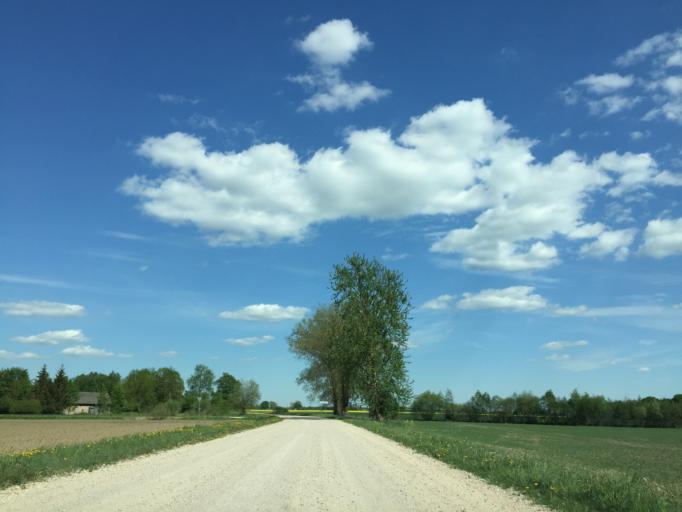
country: LV
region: Rundales
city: Pilsrundale
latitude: 56.3567
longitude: 24.0132
